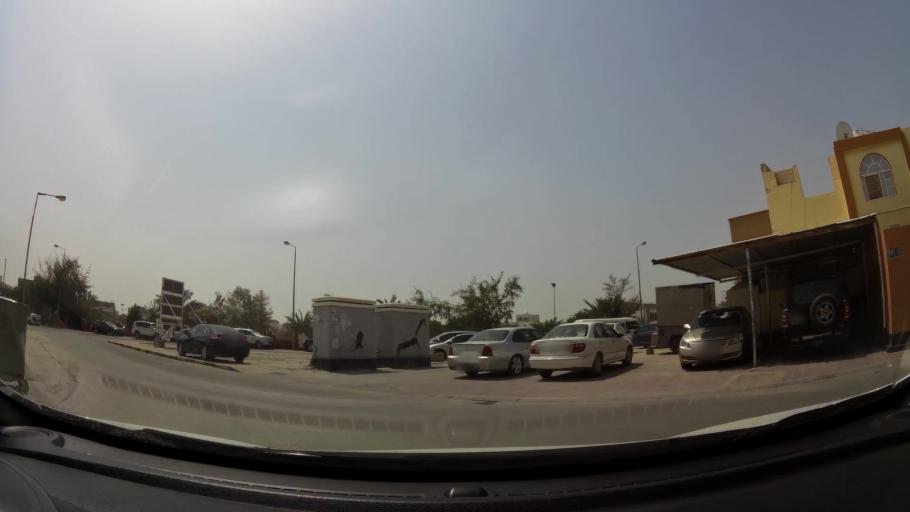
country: BH
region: Manama
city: Jidd Hafs
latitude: 26.2301
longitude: 50.4792
